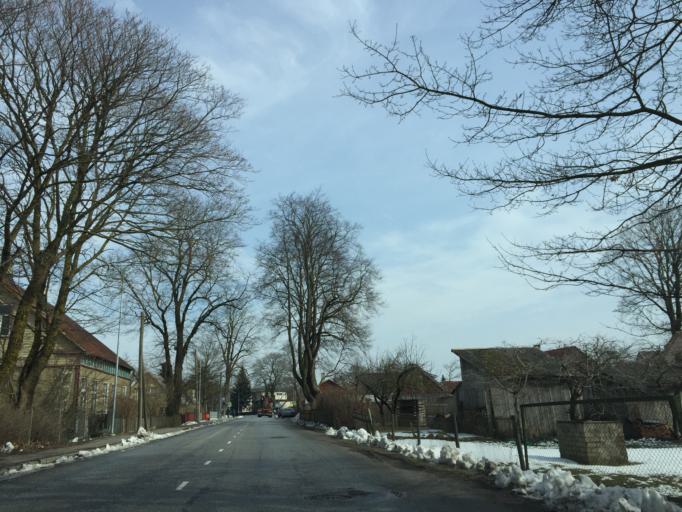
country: EE
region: Saare
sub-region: Kuressaare linn
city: Kuressaare
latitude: 58.2519
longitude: 22.4748
